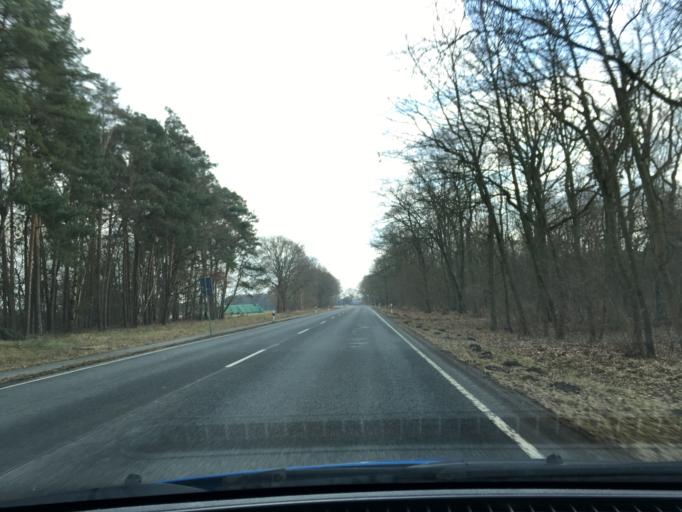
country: DE
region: Lower Saxony
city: Radbruch
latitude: 53.3385
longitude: 10.2903
